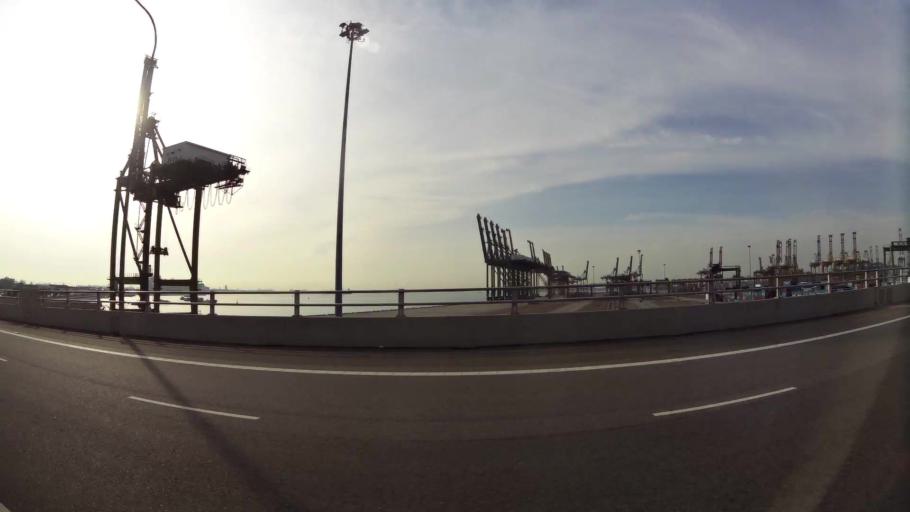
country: SG
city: Singapore
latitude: 1.2733
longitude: 103.8502
